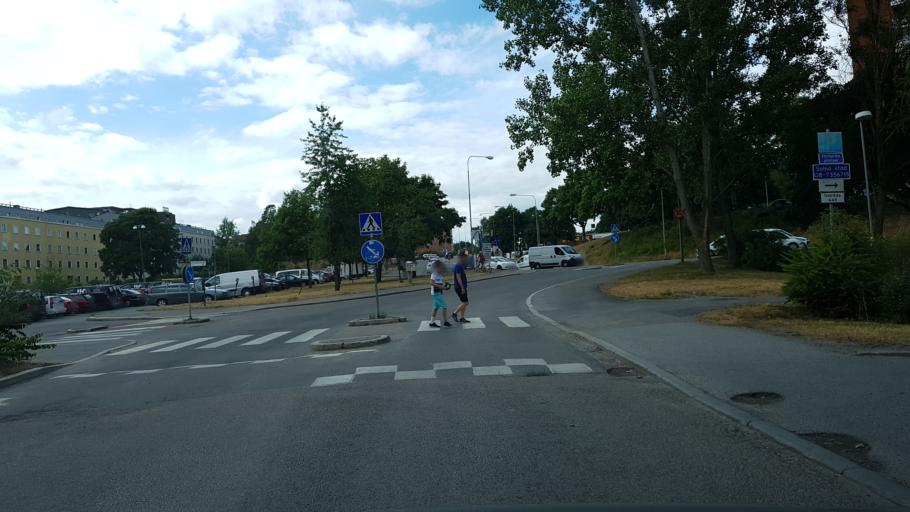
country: SE
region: Stockholm
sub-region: Solna Kommun
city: Solna
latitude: 59.3483
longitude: 17.9922
